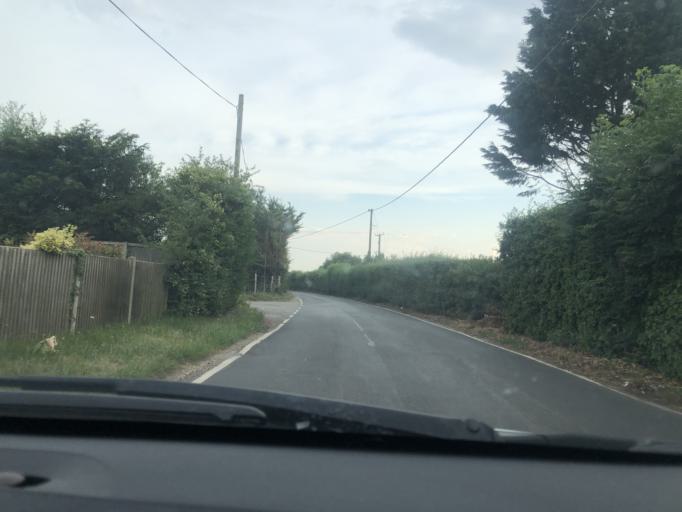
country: GB
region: England
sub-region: Kent
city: Sturry
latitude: 51.3146
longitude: 1.1384
